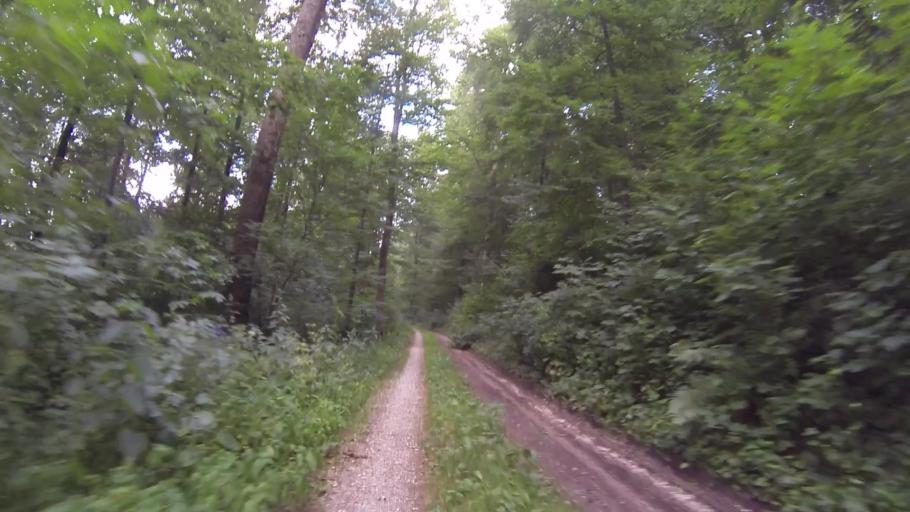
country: DE
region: Baden-Wuerttemberg
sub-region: Tuebingen Region
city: Dornstadt
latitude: 48.4410
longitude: 9.8719
